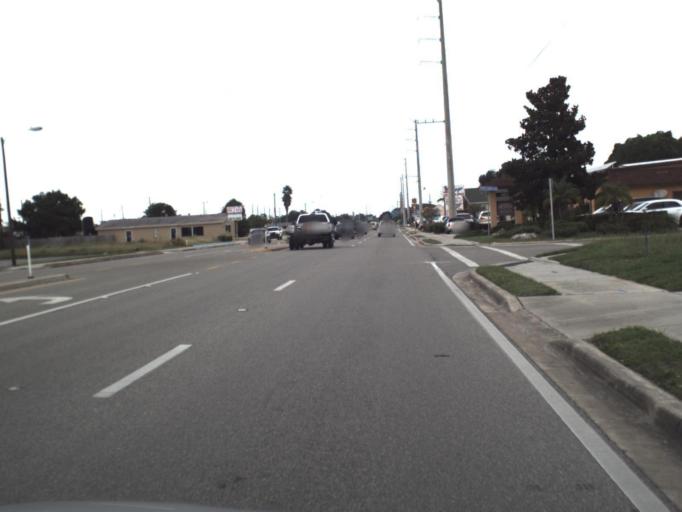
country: US
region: Florida
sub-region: Sarasota County
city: Venice
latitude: 27.0945
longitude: -82.4335
